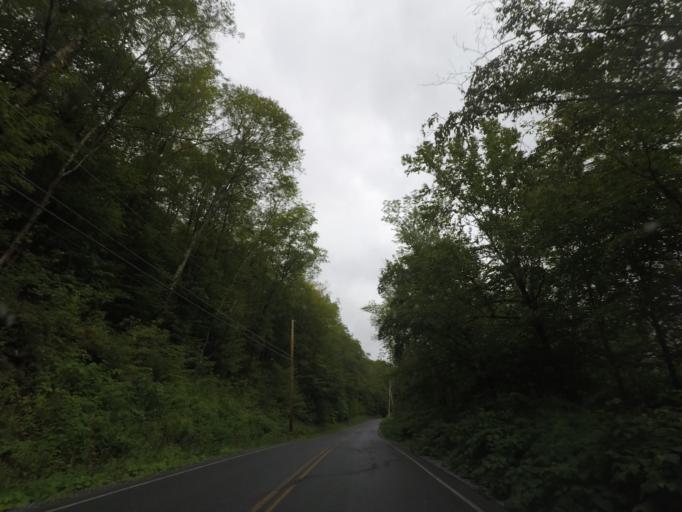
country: US
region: New York
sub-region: Rensselaer County
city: Averill Park
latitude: 42.6924
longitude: -73.3900
